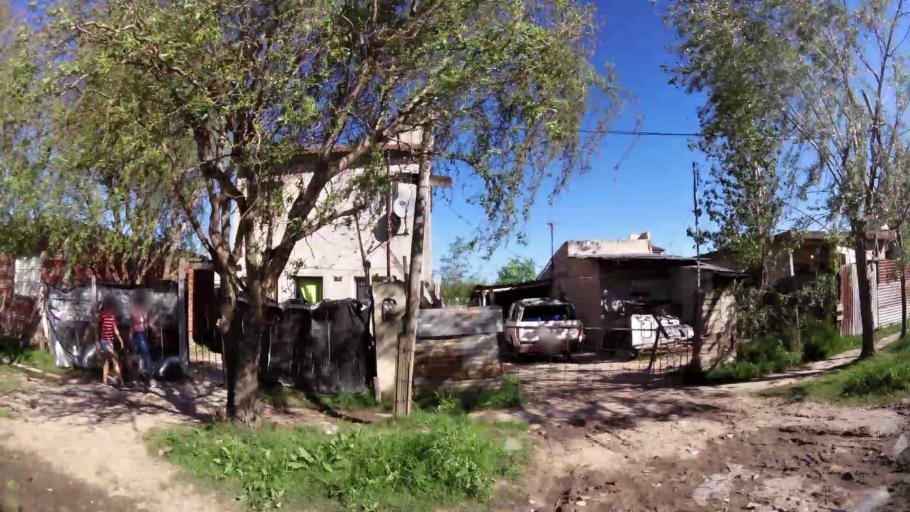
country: AR
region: Buenos Aires
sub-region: Partido de Quilmes
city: Quilmes
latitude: -34.7597
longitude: -58.3176
